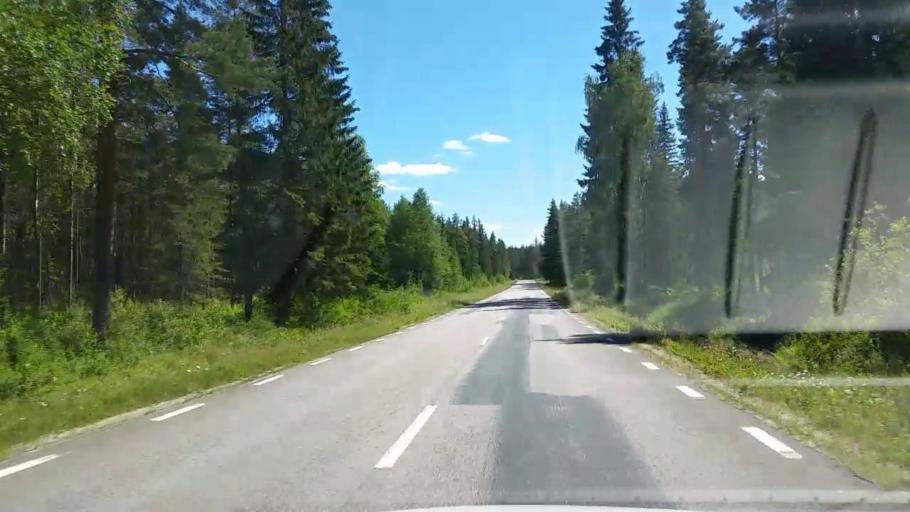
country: SE
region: Gaevleborg
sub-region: Ovanakers Kommun
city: Edsbyn
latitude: 61.3442
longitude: 15.8196
